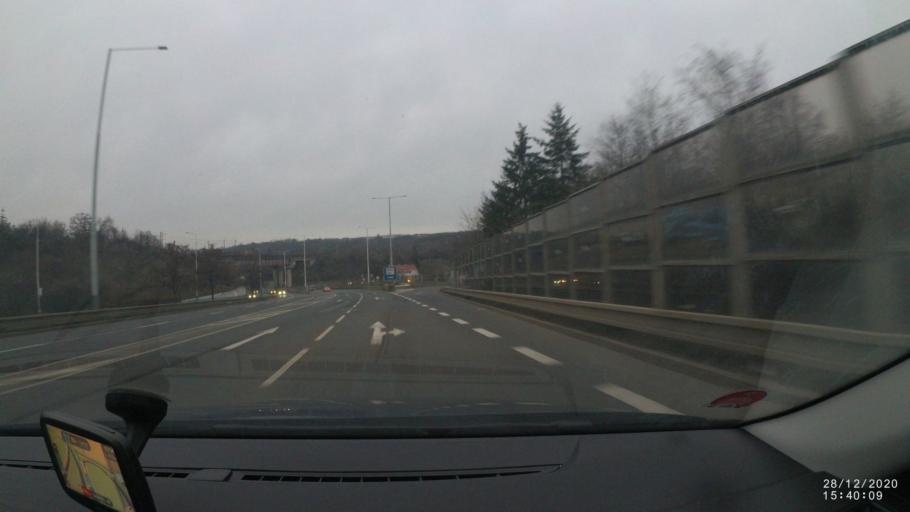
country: CZ
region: Praha
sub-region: Praha 8
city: Liben
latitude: 50.1066
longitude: 14.4816
